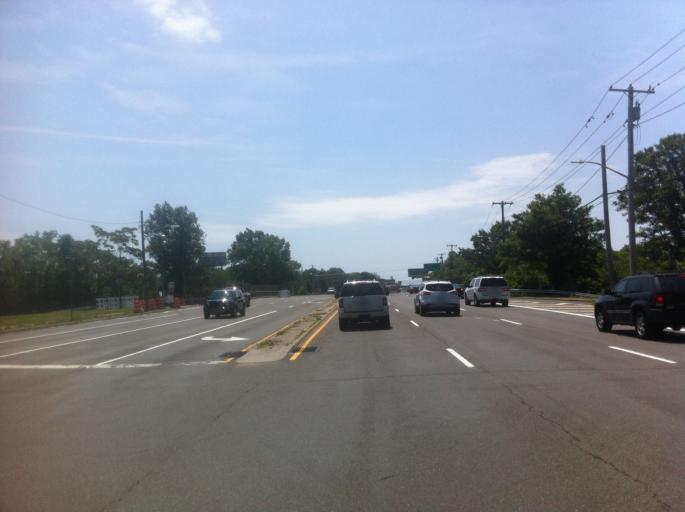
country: US
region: New York
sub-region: Nassau County
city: Jericho
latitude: 40.7869
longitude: -73.5347
